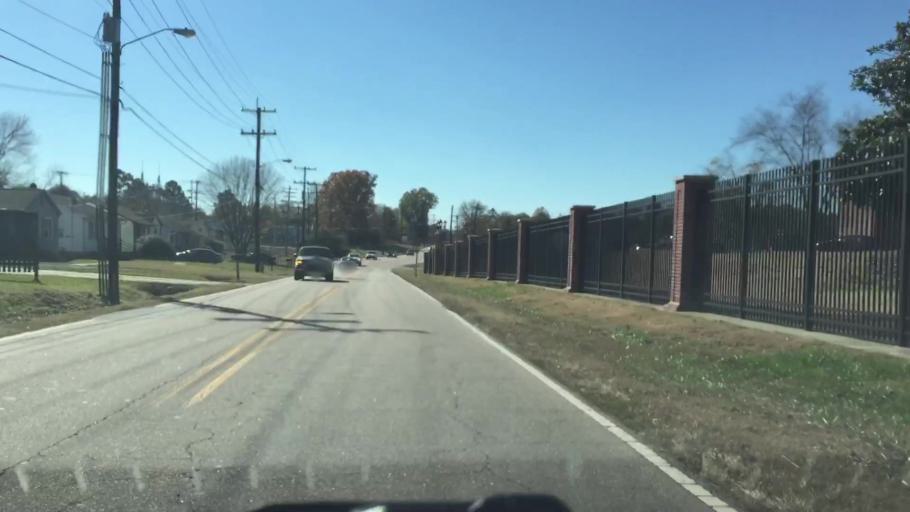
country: US
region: North Carolina
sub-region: Rowan County
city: Salisbury
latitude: 35.6816
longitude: -80.4870
